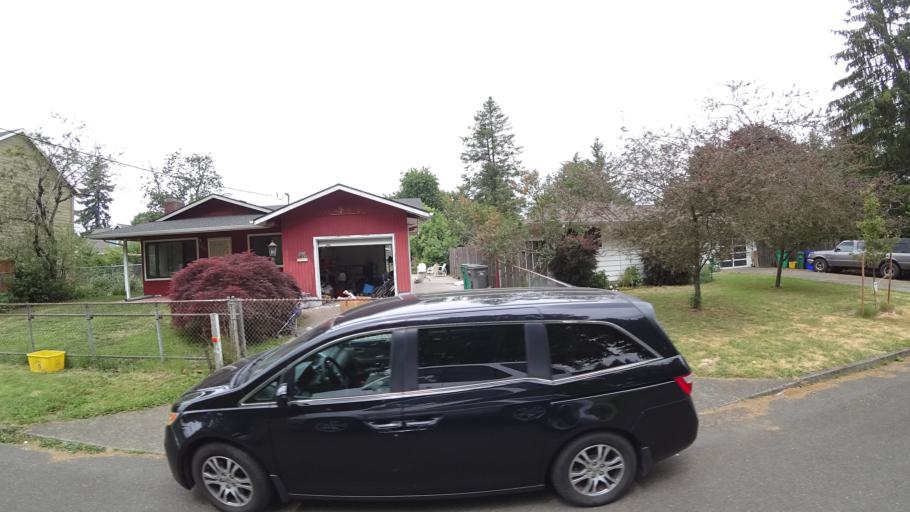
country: US
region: Oregon
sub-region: Multnomah County
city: Lents
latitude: 45.4867
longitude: -122.5599
